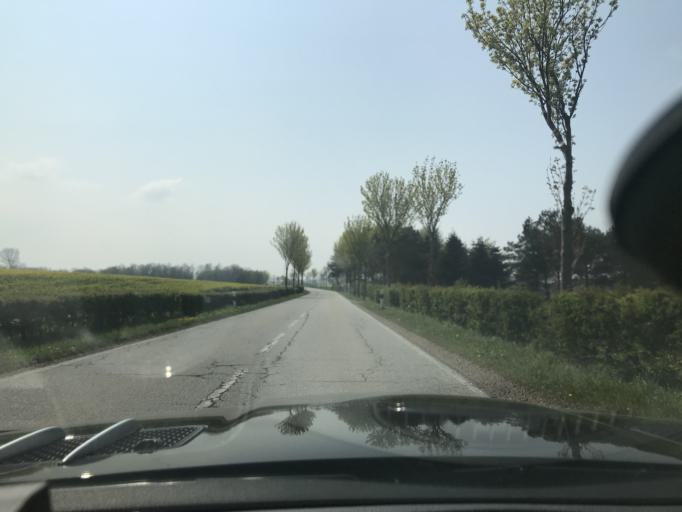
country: DE
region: Schleswig-Holstein
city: Heiligenhafen
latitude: 54.3659
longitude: 10.9503
